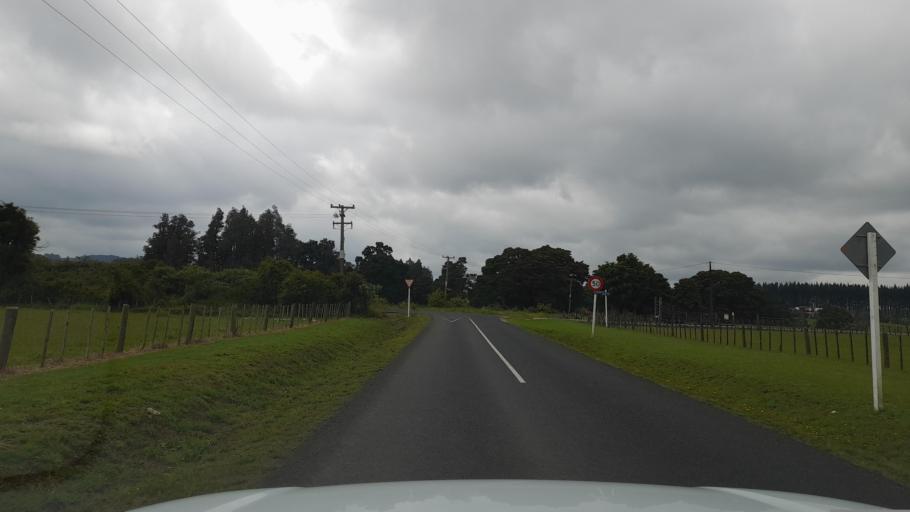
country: NZ
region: Northland
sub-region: Far North District
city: Waimate North
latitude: -35.4198
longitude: 173.7954
